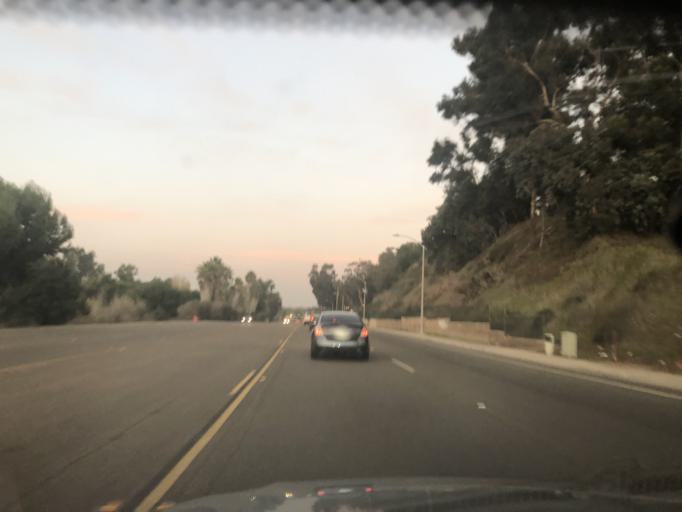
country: US
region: California
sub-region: San Diego County
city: Bonita
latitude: 32.6547
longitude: -117.0453
